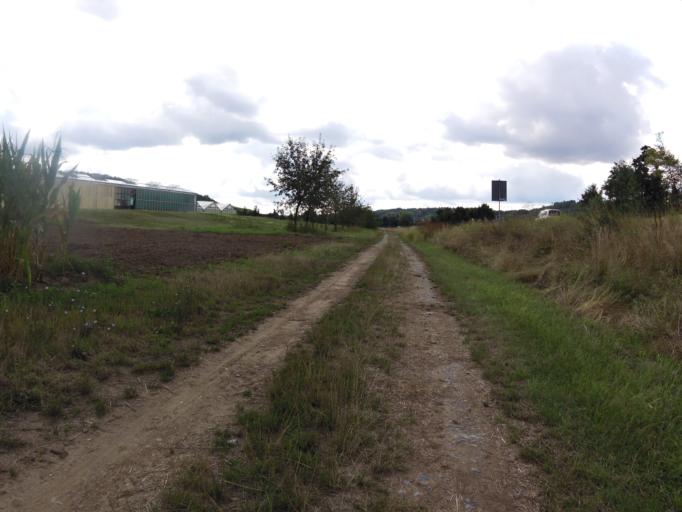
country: DE
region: Bavaria
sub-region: Regierungsbezirk Unterfranken
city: Sommerhausen
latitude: 49.6936
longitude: 10.0246
